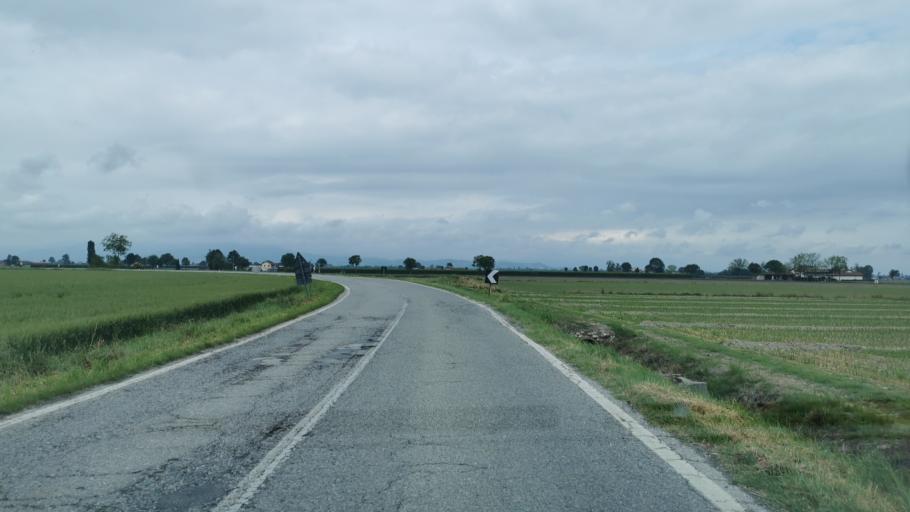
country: IT
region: Piedmont
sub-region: Provincia di Cuneo
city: Genola
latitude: 44.6106
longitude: 7.6129
